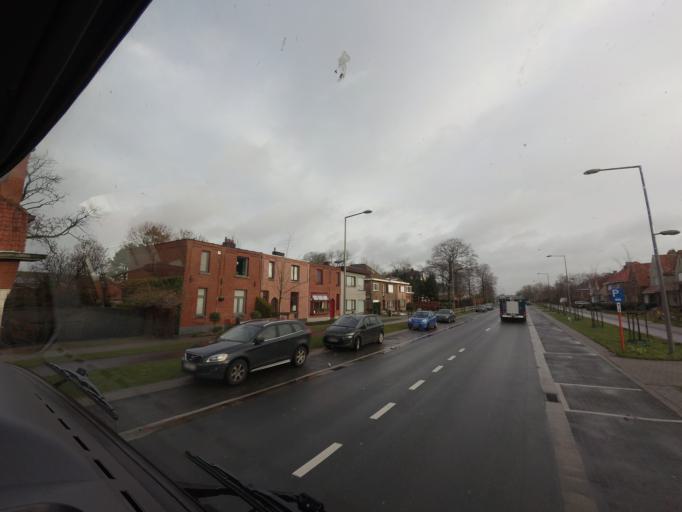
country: BE
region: Flanders
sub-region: Provincie Antwerpen
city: Stabroek
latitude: 51.3360
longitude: 4.3746
